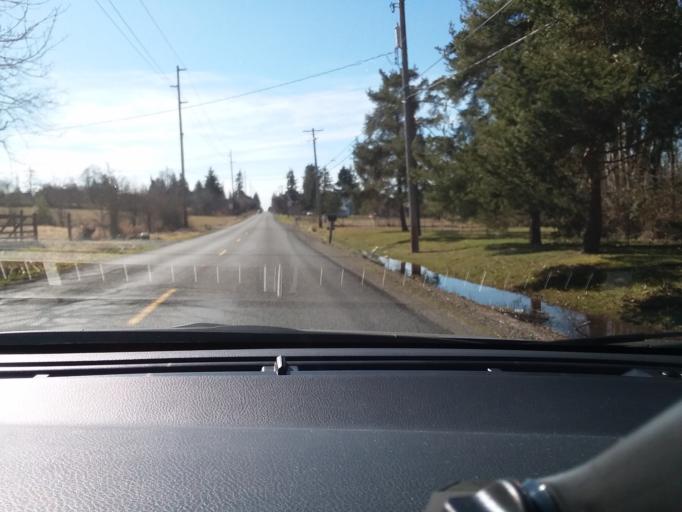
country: US
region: Washington
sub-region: Pierce County
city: Summit
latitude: 47.1759
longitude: -122.3785
